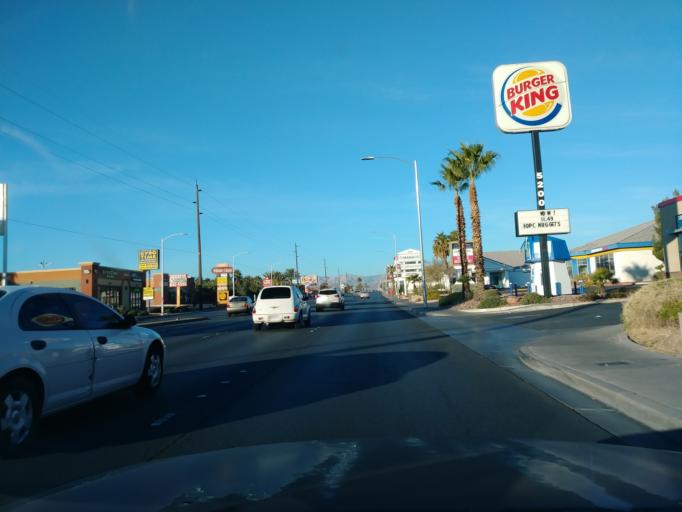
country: US
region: Nevada
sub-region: Clark County
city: Spring Valley
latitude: 36.1593
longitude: -115.2118
